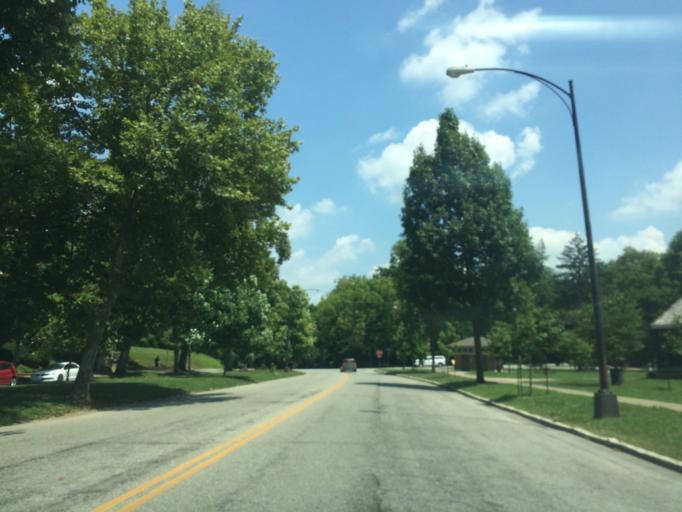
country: US
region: Kentucky
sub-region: Jefferson County
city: Audubon Park
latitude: 38.2362
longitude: -85.7106
